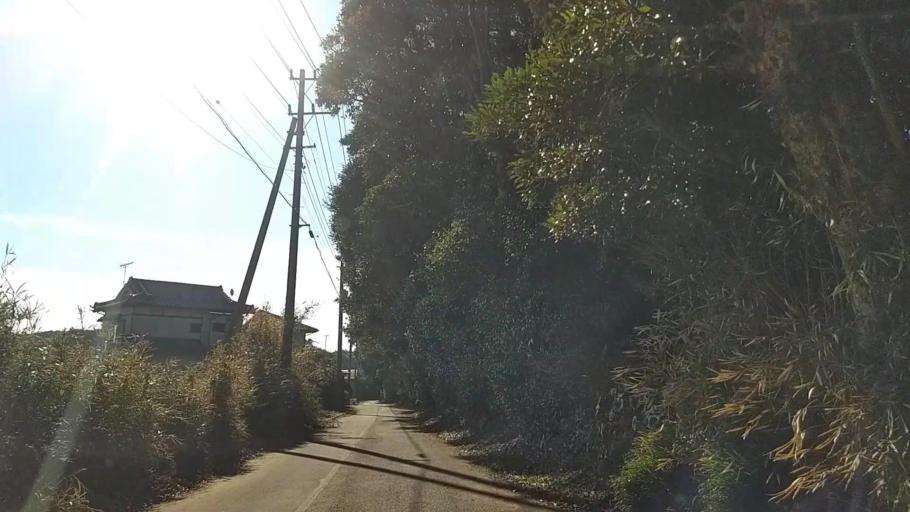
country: JP
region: Chiba
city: Hasaki
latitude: 35.7053
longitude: 140.8480
